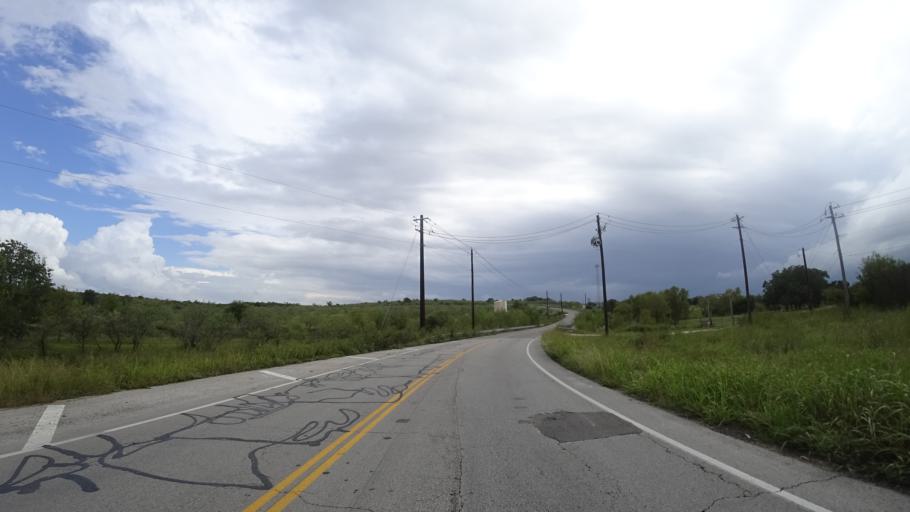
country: US
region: Texas
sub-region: Travis County
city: Onion Creek
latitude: 30.1547
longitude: -97.7353
